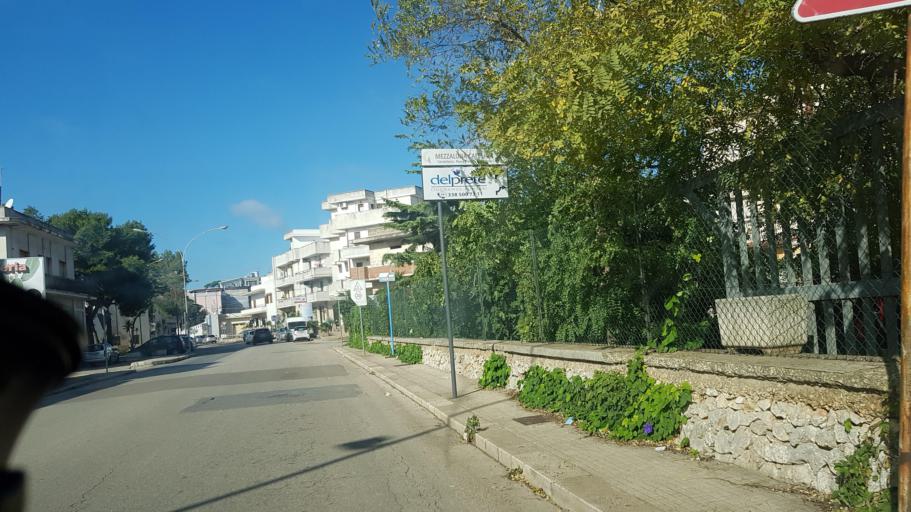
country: IT
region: Apulia
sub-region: Provincia di Brindisi
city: Carovigno
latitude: 40.7012
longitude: 17.6632
